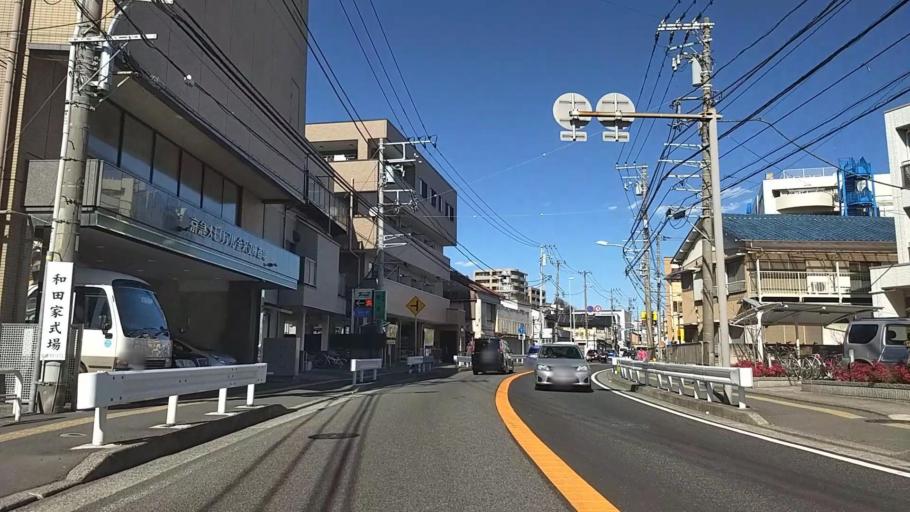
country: JP
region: Kanagawa
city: Zushi
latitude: 35.3448
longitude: 139.6224
